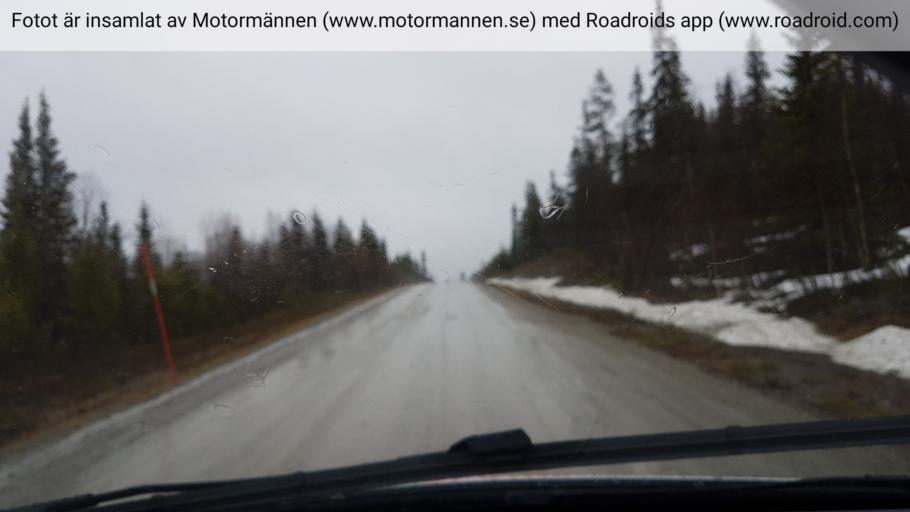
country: SE
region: Jaemtland
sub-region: Are Kommun
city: Are
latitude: 62.6389
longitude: 13.0775
